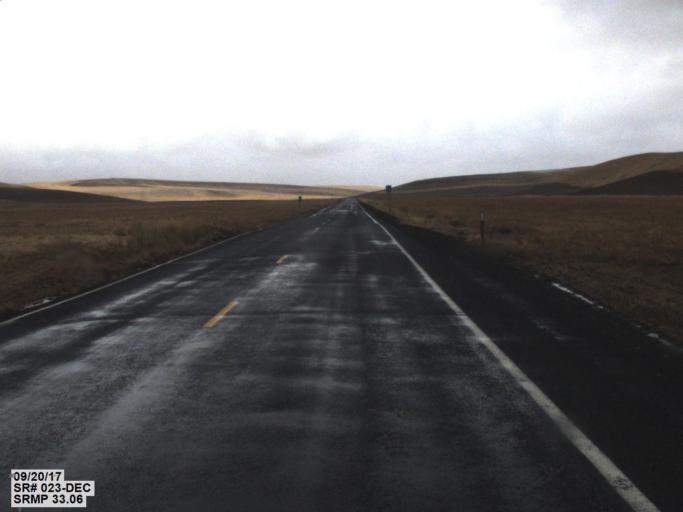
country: US
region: Washington
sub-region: Spokane County
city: Cheney
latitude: 47.1825
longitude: -117.8711
